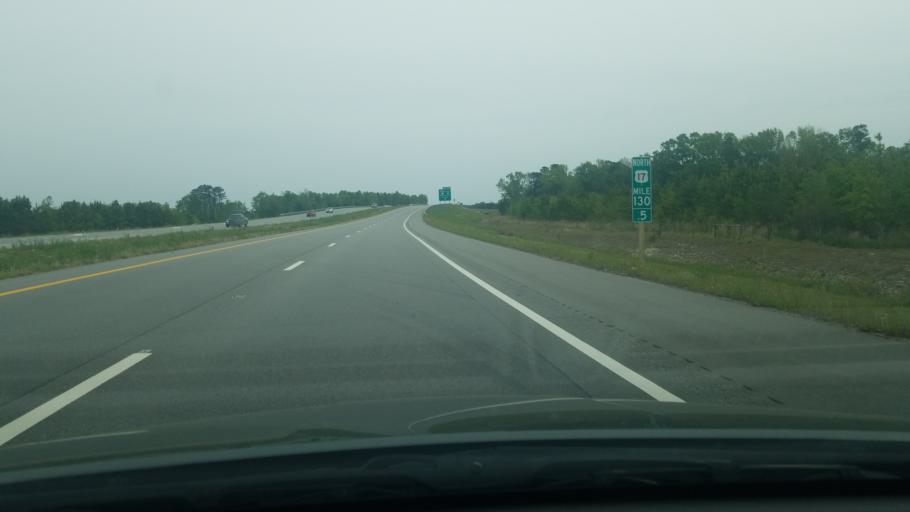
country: US
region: North Carolina
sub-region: Jones County
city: Maysville
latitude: 34.9954
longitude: -77.2342
